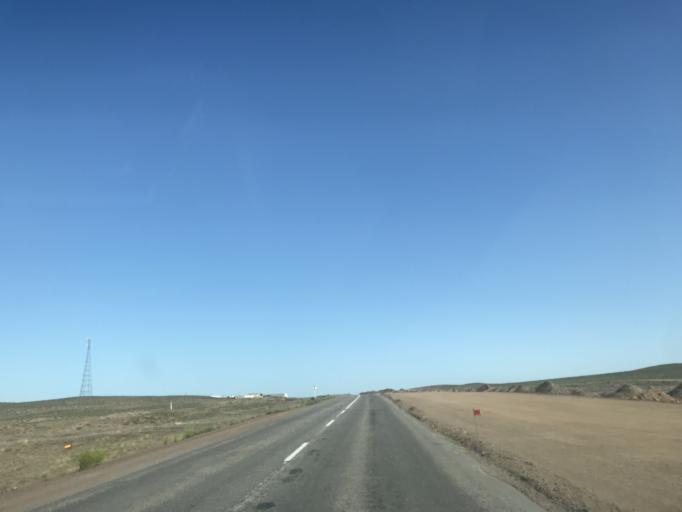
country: KZ
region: Zhambyl
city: Mynaral
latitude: 45.3301
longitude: 73.7275
